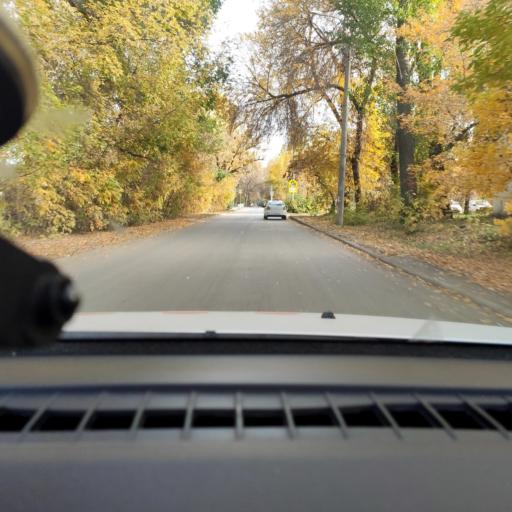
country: RU
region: Samara
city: Samara
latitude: 53.1198
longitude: 50.0770
